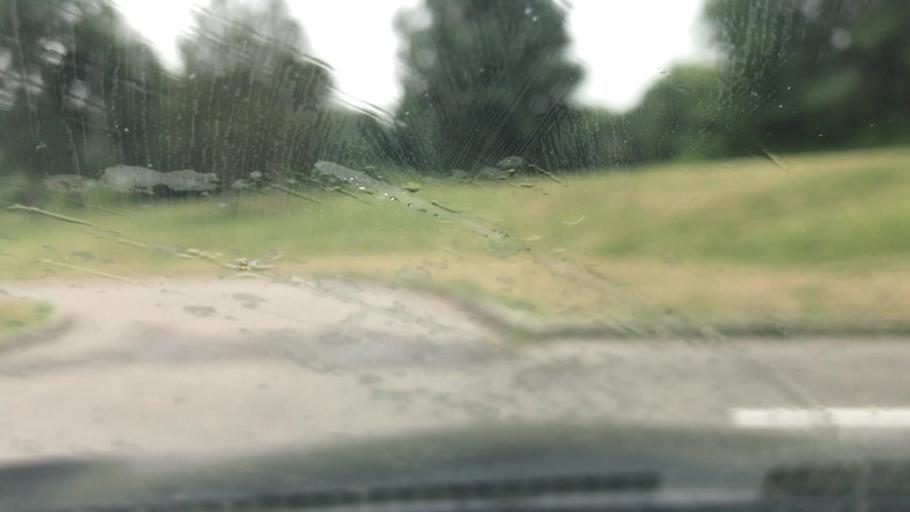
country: US
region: Michigan
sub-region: Oakland County
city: South Lyon
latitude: 42.5108
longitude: -83.6747
